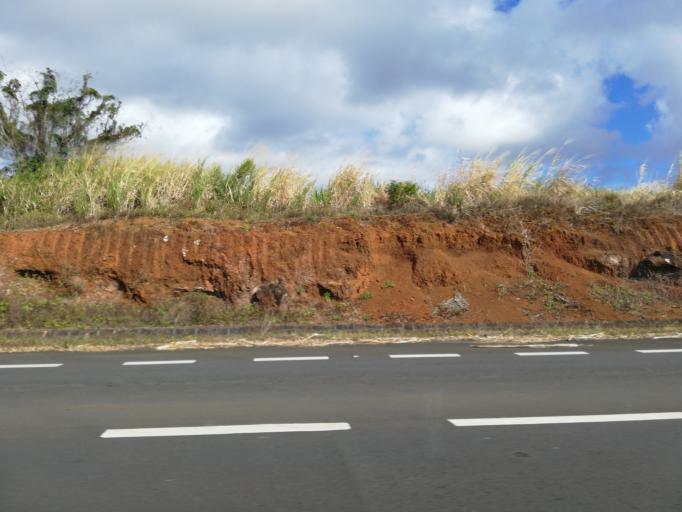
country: MU
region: Grand Port
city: Mahebourg
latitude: -20.4021
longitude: 57.6801
